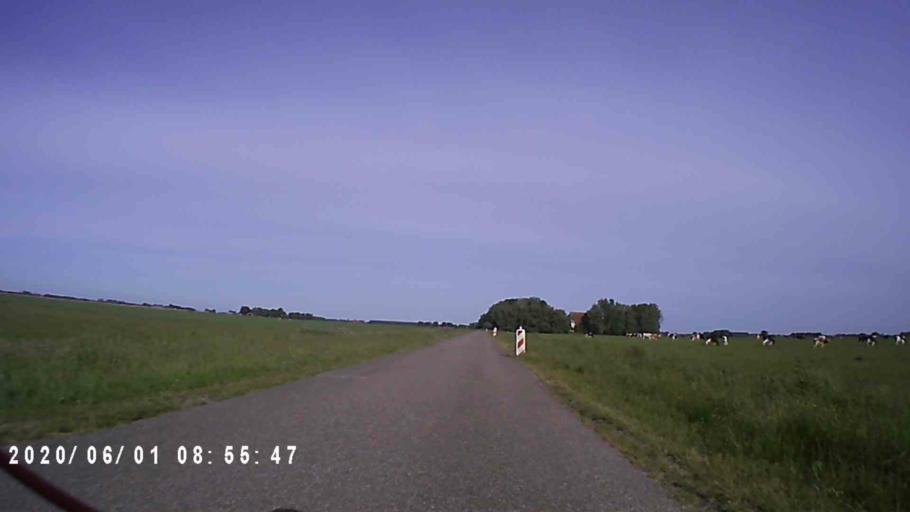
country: NL
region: Friesland
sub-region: Gemeente Leeuwarderadeel
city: Britsum
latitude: 53.2787
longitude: 5.8225
